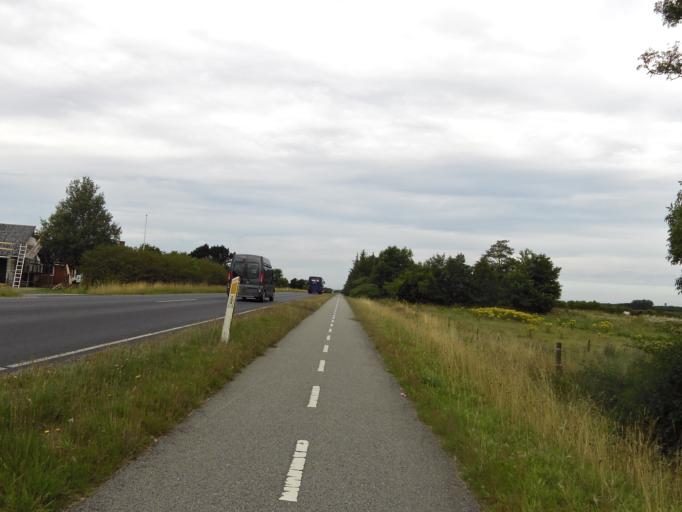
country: DK
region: South Denmark
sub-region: Esbjerg Kommune
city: Ribe
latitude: 55.3148
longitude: 8.7861
